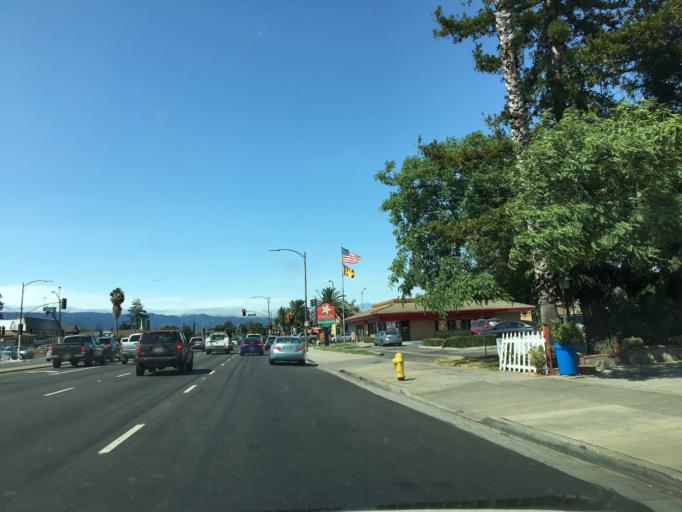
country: US
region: California
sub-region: Santa Clara County
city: Cambrian Park
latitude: 37.2619
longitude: -121.9304
